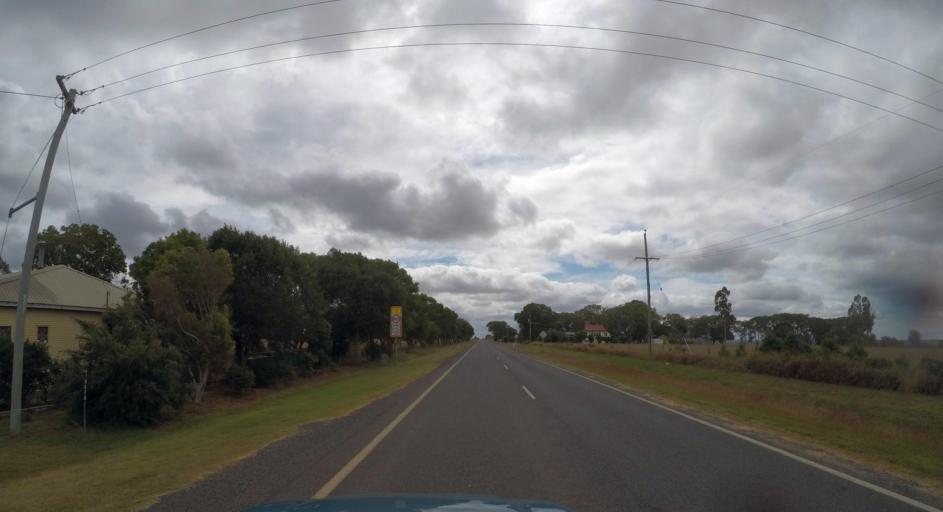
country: AU
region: Queensland
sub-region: South Burnett
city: Kingaroy
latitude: -26.3939
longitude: 151.2439
